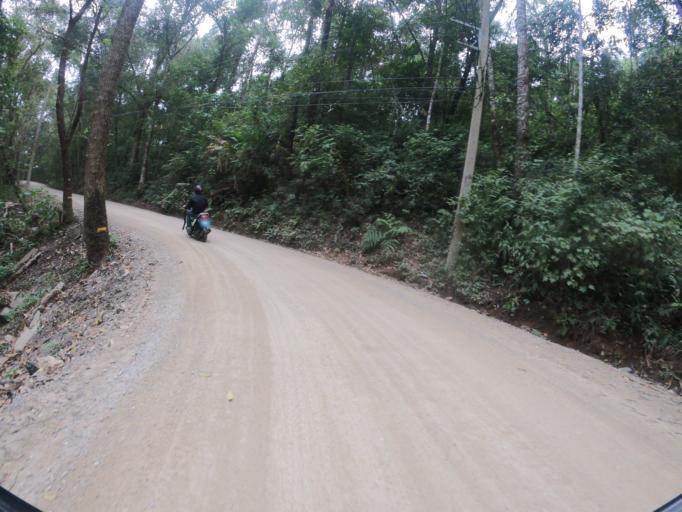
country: TH
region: Chiang Mai
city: Chiang Mai
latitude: 18.8145
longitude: 98.8899
